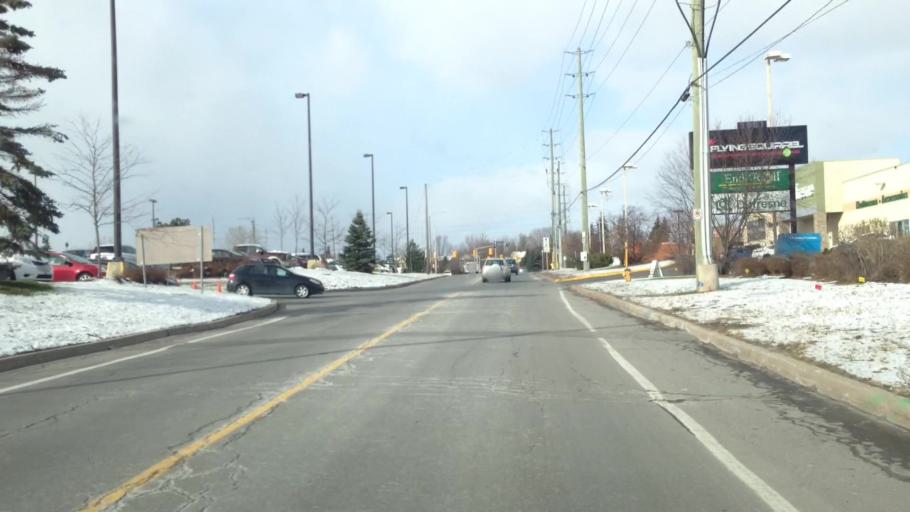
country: CA
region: Ontario
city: Ottawa
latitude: 45.4146
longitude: -75.6012
